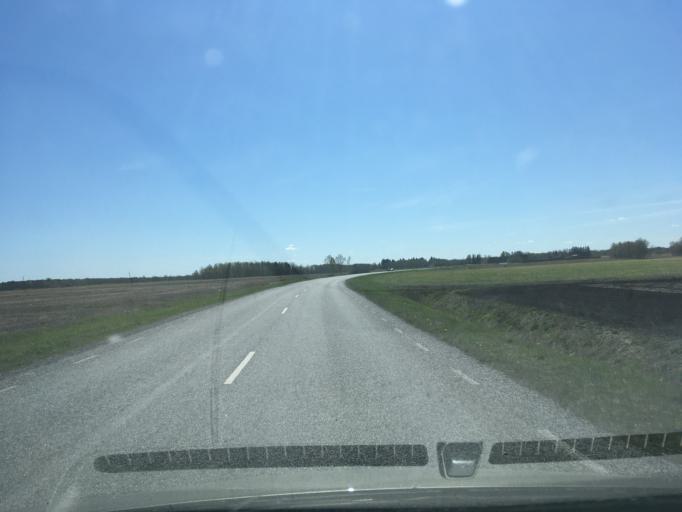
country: EE
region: Harju
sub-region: Raasiku vald
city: Arukula
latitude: 59.4198
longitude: 25.0780
